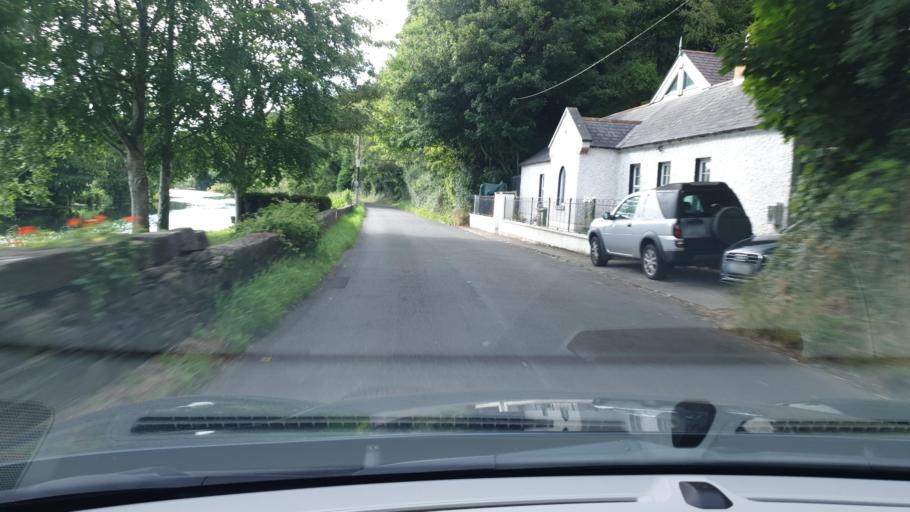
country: IE
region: Leinster
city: Castleknock
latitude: 53.3616
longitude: -6.3653
